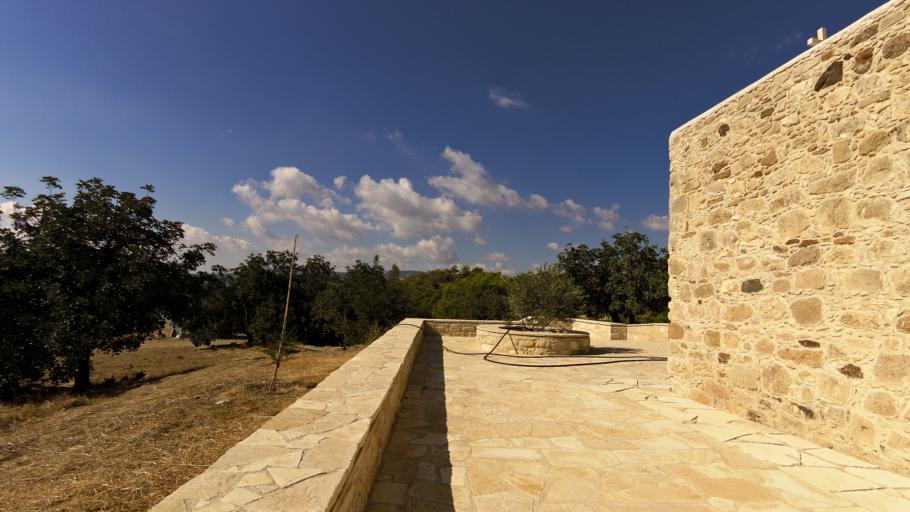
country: CY
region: Limassol
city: Parekklisha
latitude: 34.7596
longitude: 33.1334
